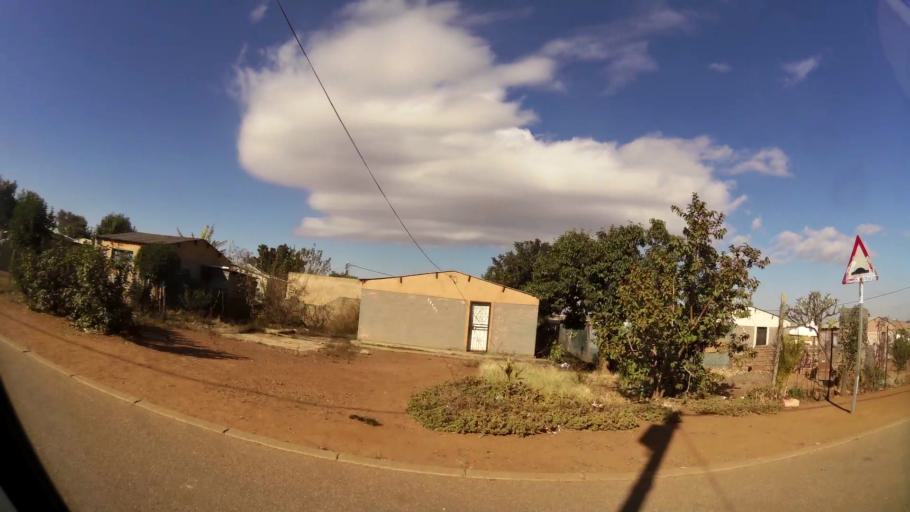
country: ZA
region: Gauteng
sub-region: City of Tshwane Metropolitan Municipality
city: Cullinan
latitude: -25.6967
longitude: 28.4104
